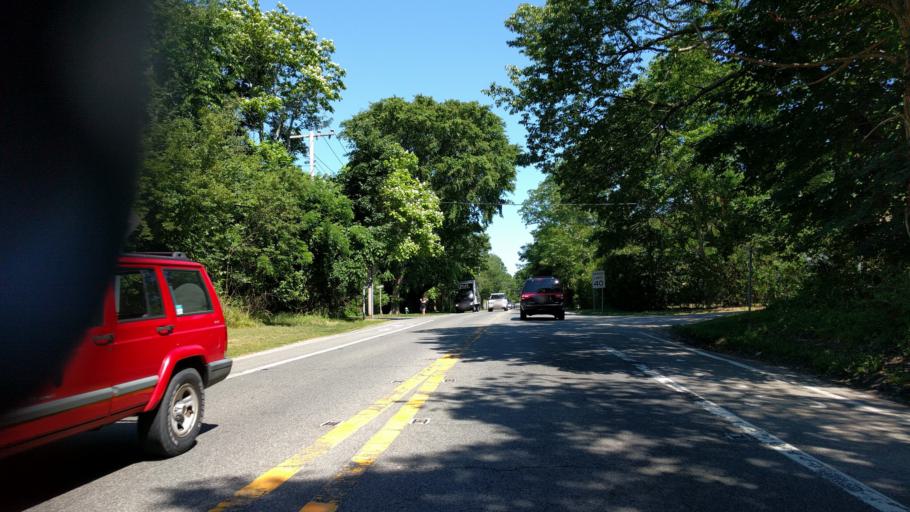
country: US
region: New York
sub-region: Suffolk County
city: Sag Harbor
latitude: 41.0128
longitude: -72.3124
